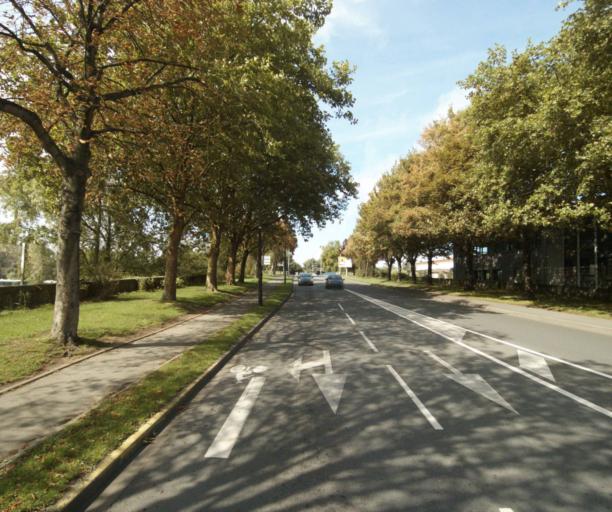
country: FR
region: Nord-Pas-de-Calais
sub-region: Departement du Nord
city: Lambersart
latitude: 50.6307
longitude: 3.0344
